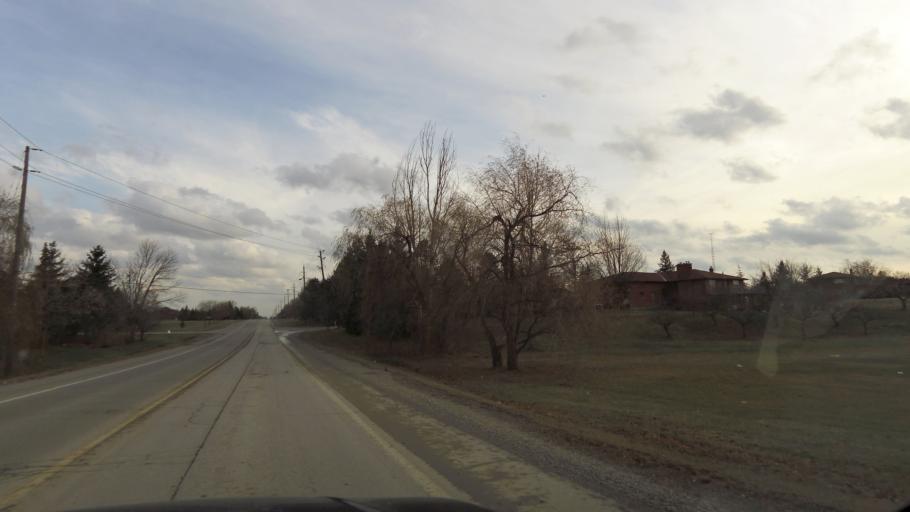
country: CA
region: Ontario
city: Brampton
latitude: 43.7961
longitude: -79.7189
